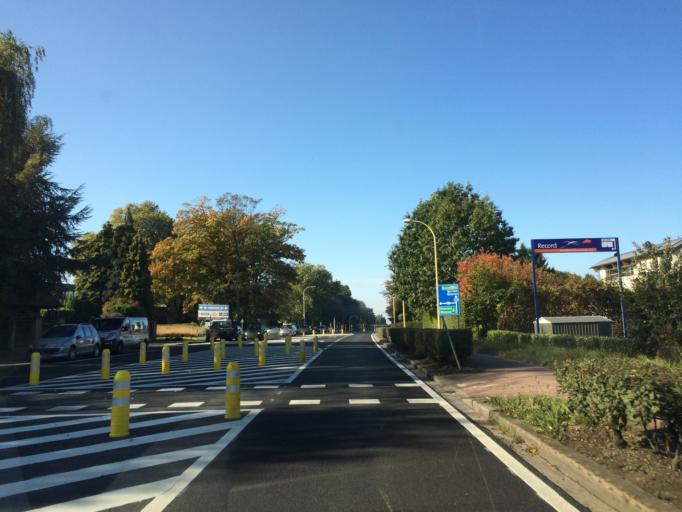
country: BE
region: Flanders
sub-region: Provincie Vlaams-Brabant
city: Meise
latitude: 50.9440
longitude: 4.3285
